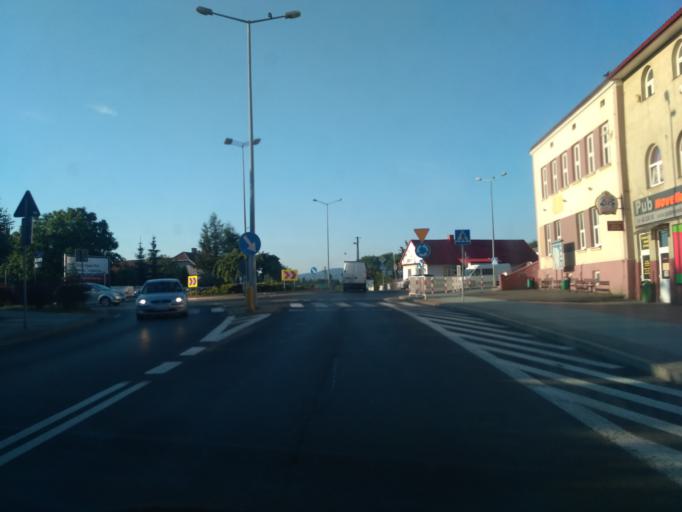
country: PL
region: Subcarpathian Voivodeship
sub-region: Powiat krosnienski
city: Miejsce Piastowe
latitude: 49.6351
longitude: 21.7867
